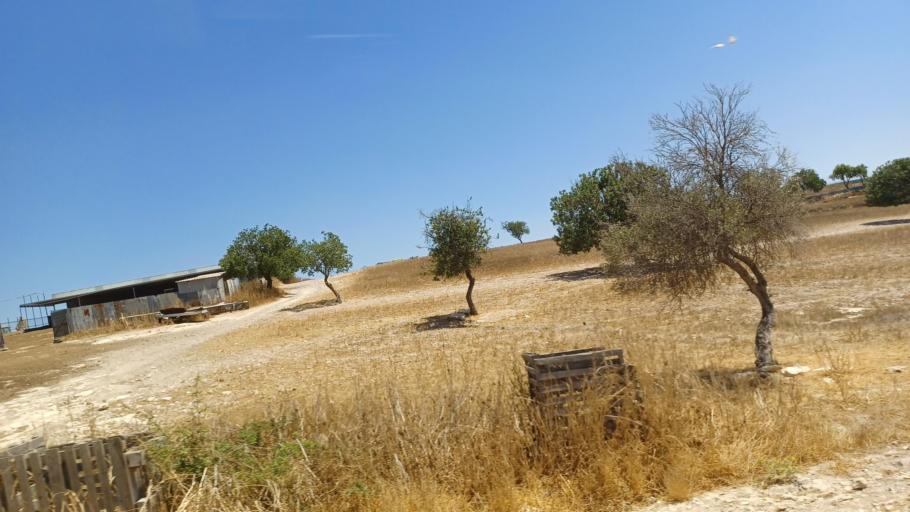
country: CY
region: Lefkosia
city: Lympia
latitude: 34.9868
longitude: 33.4761
